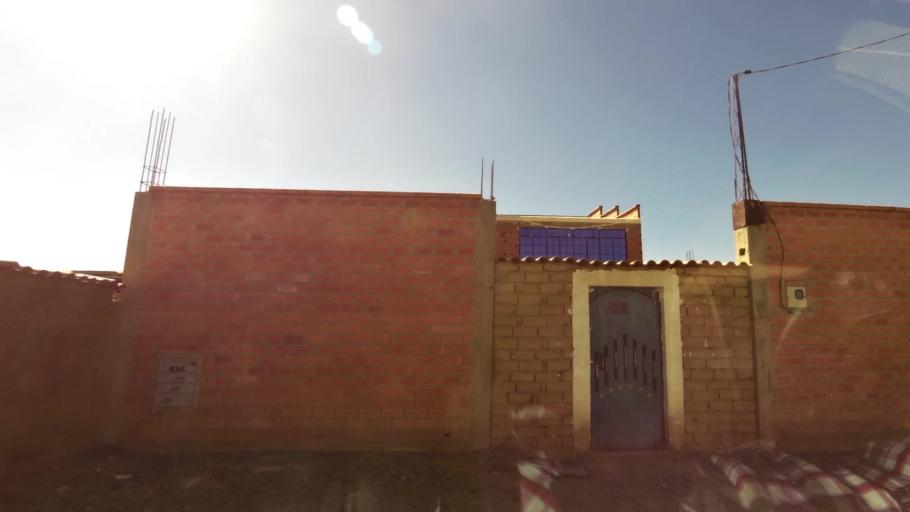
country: BO
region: La Paz
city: La Paz
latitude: -16.5366
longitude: -68.2250
